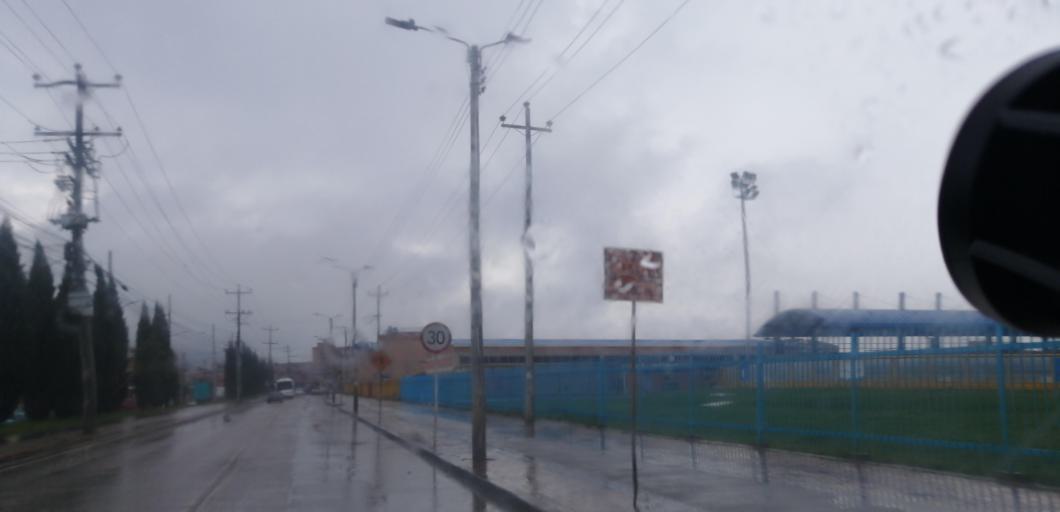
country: CO
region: Cundinamarca
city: Madrid
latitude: 4.7377
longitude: -74.2559
